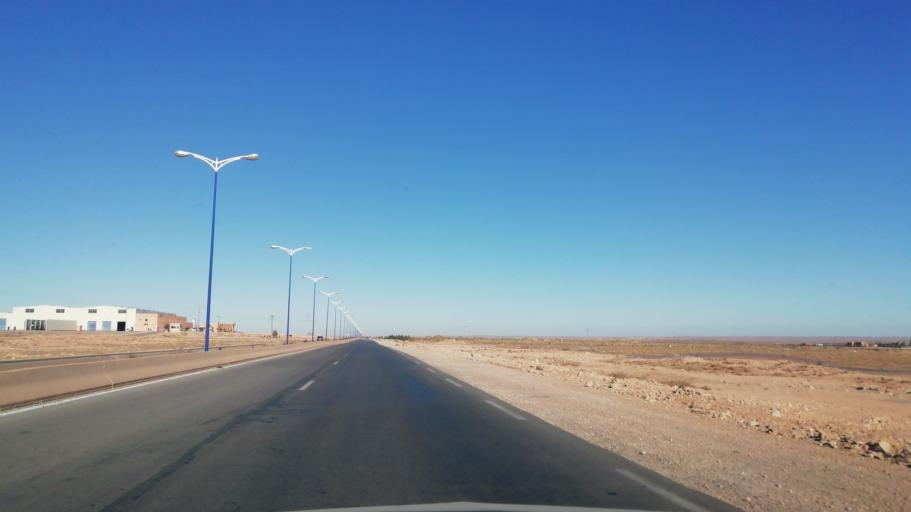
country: DZ
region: Wilaya de Naama
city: Naama
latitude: 33.5444
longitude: -0.2503
